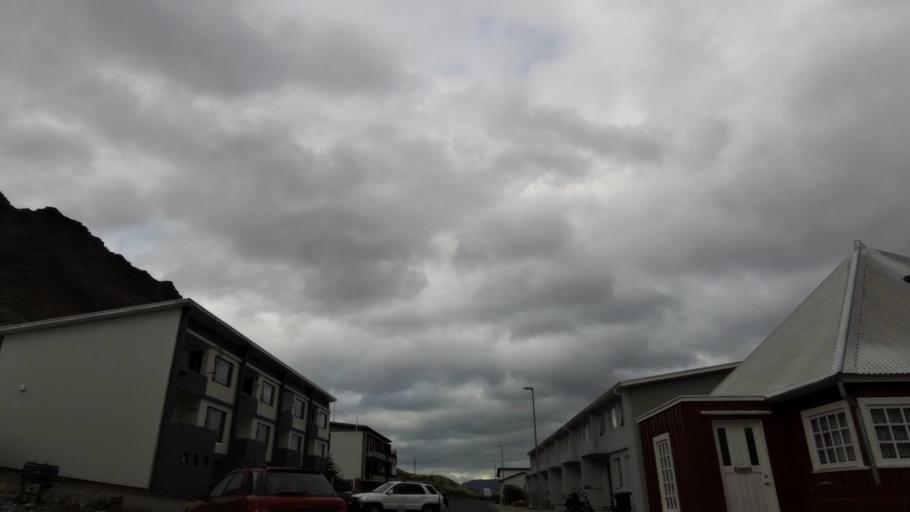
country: IS
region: Westfjords
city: Isafjoerdur
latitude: 66.0789
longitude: -23.1264
